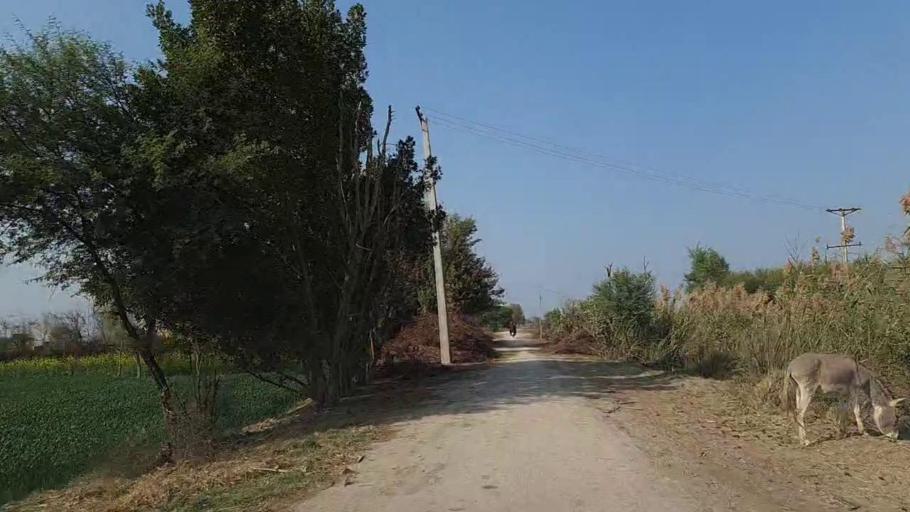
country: PK
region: Sindh
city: Jam Sahib
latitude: 26.2890
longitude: 68.5649
